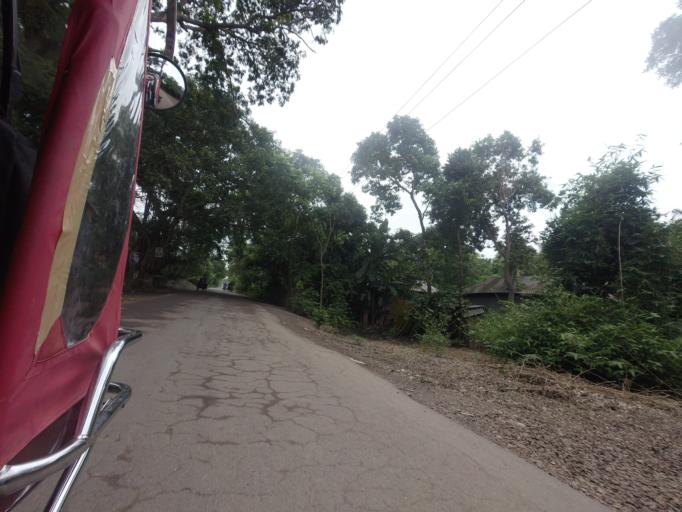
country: BD
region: Khulna
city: Kalia
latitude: 23.1953
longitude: 89.6827
